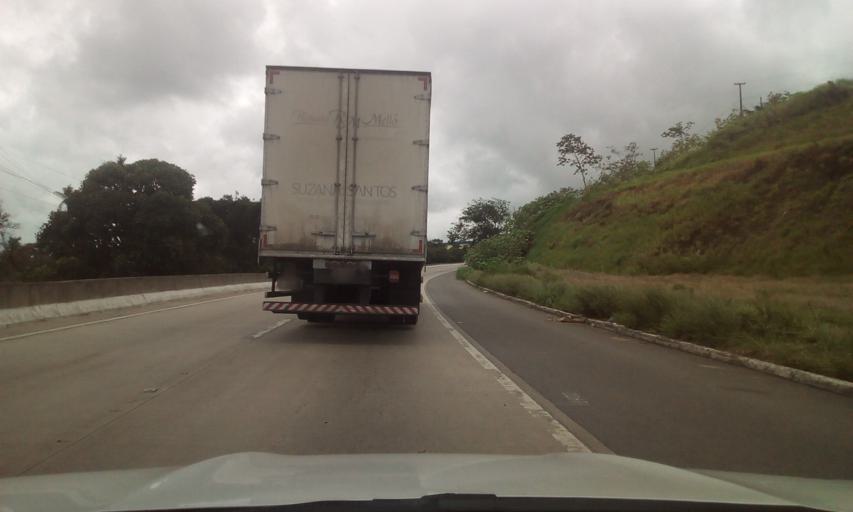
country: BR
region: Pernambuco
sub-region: Igarassu
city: Igarassu
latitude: -7.8062
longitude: -34.9249
